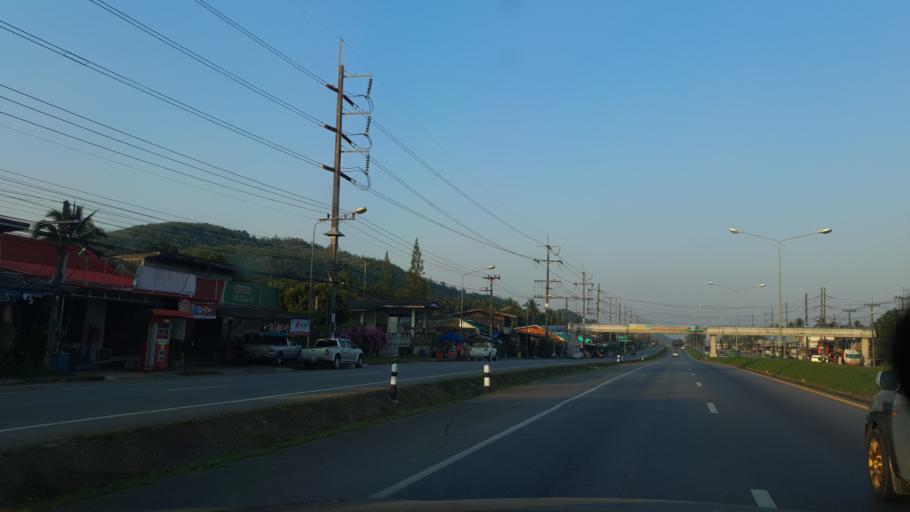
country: TH
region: Prachuap Khiri Khan
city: Thap Sakae
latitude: 11.3804
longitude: 99.5039
